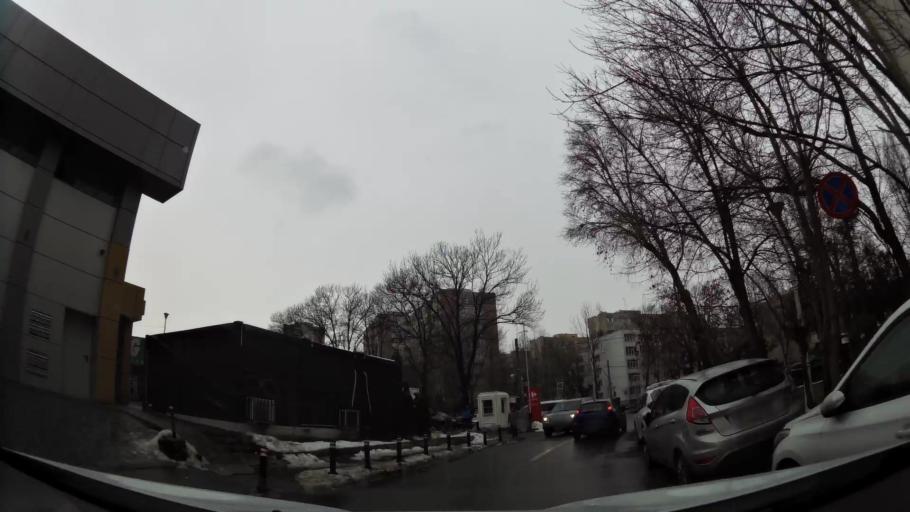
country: RO
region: Ilfov
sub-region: Comuna Chiajna
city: Rosu
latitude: 44.4173
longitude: 26.0284
